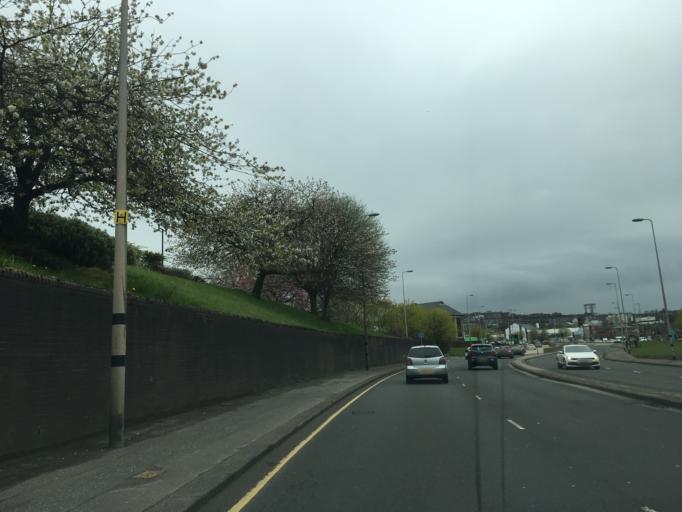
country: GB
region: Scotland
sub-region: Inverclyde
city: Greenock
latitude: 55.9434
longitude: -4.7401
